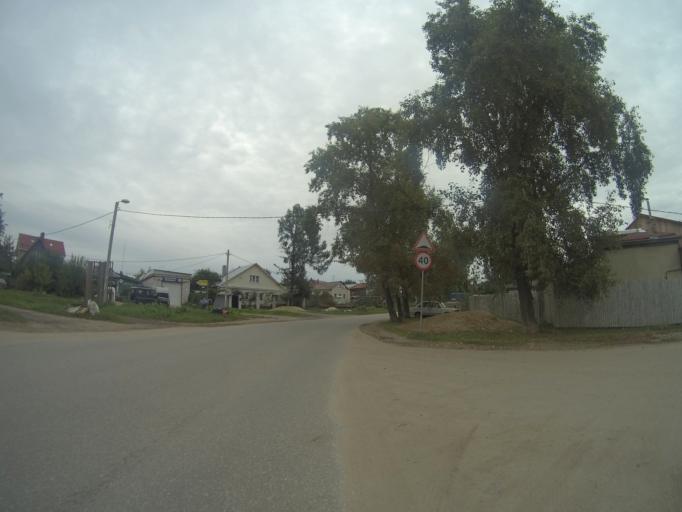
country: RU
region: Vladimir
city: Vladimir
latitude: 56.1123
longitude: 40.3603
